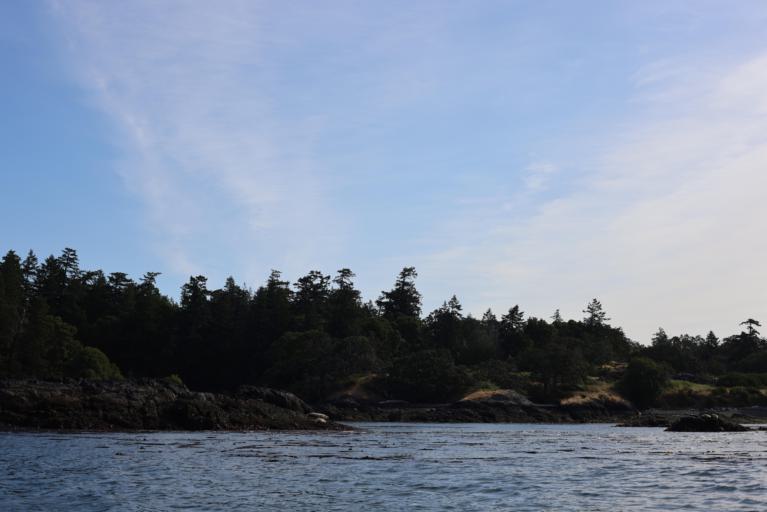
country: CA
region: British Columbia
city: Metchosin
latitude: 48.3381
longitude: -123.5480
